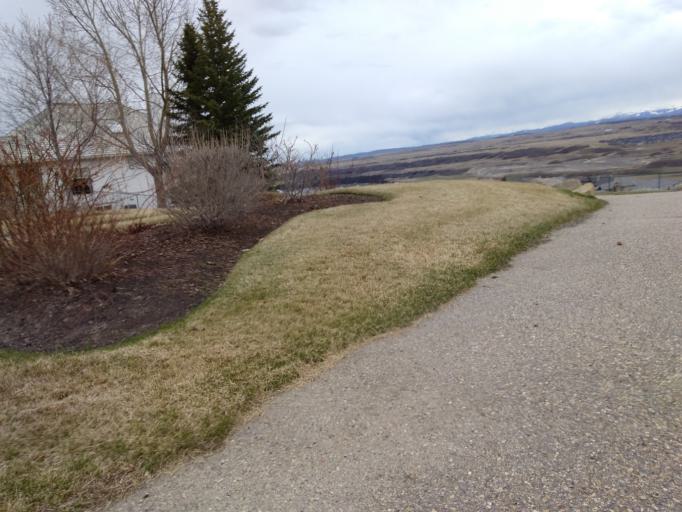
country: CA
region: Alberta
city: Cochrane
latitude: 51.1856
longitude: -114.4278
